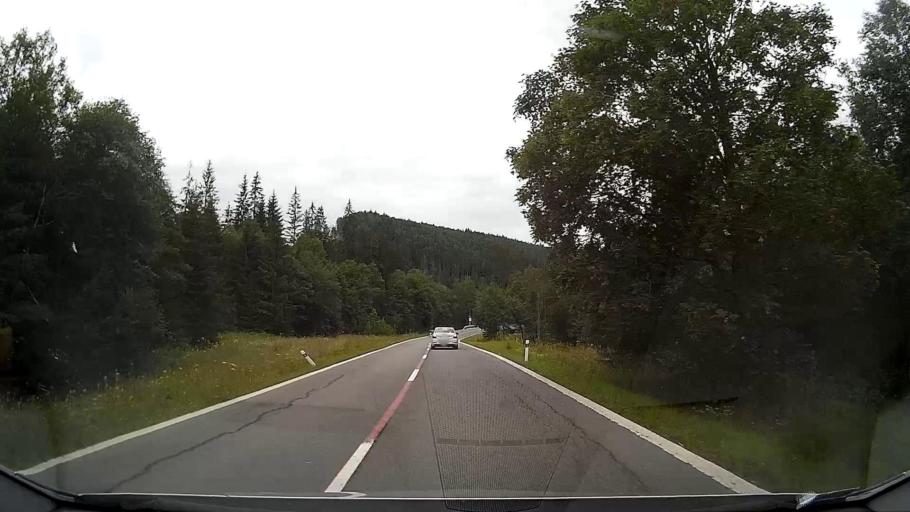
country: SK
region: Banskobystricky
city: Revuca
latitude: 48.8214
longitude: 20.1459
